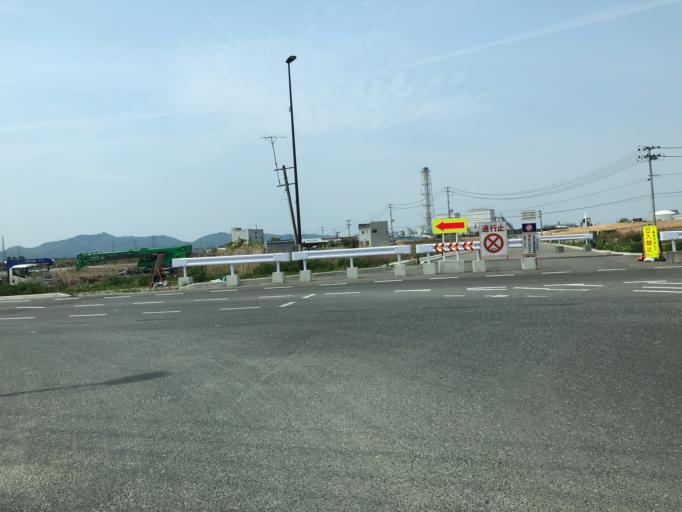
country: JP
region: Miyagi
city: Marumori
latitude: 37.8299
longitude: 140.9562
